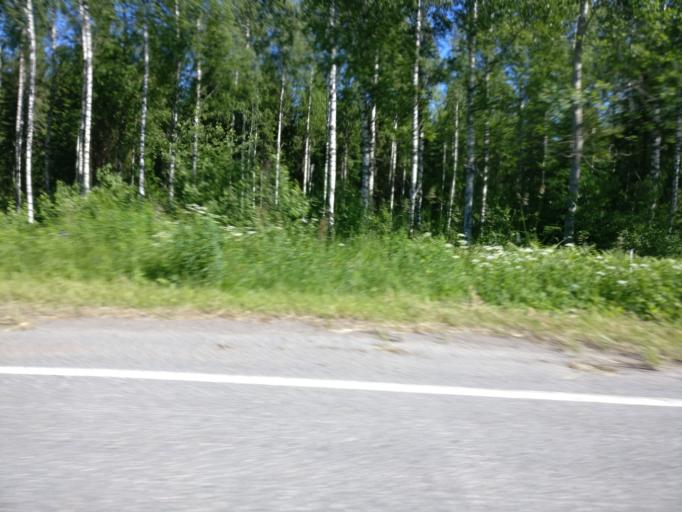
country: FI
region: Southern Savonia
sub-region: Savonlinna
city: Rantasalmi
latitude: 62.1075
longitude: 28.2569
